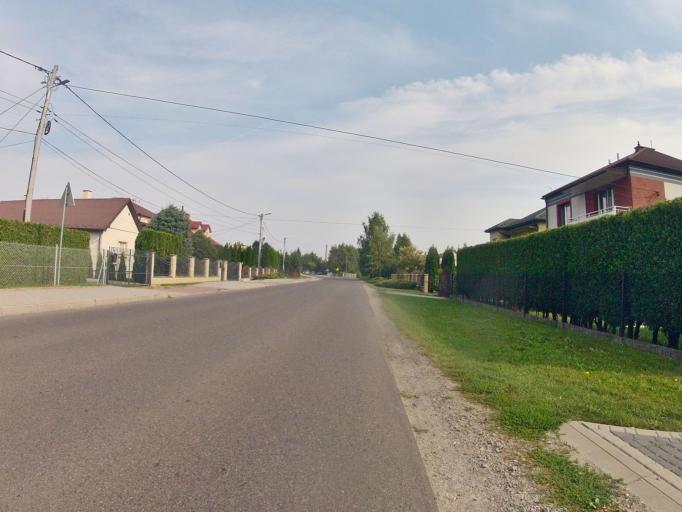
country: PL
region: Subcarpathian Voivodeship
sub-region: Powiat jasielski
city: Debowiec
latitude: 49.7128
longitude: 21.4619
